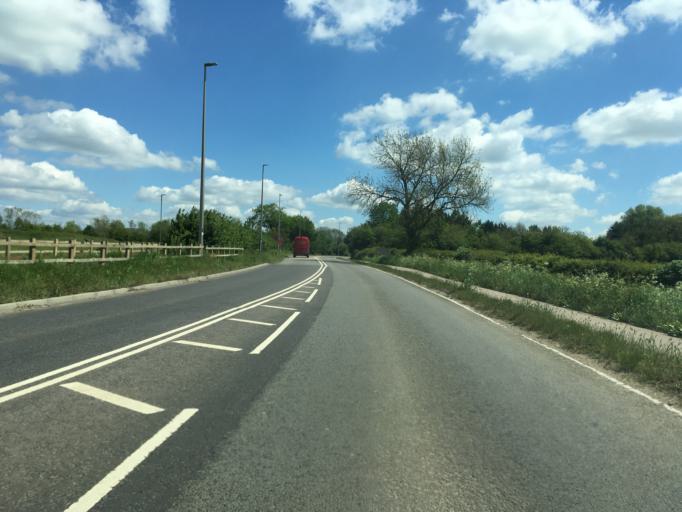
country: GB
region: England
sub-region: Milton Keynes
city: Wavendon
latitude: 52.0287
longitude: -0.6718
